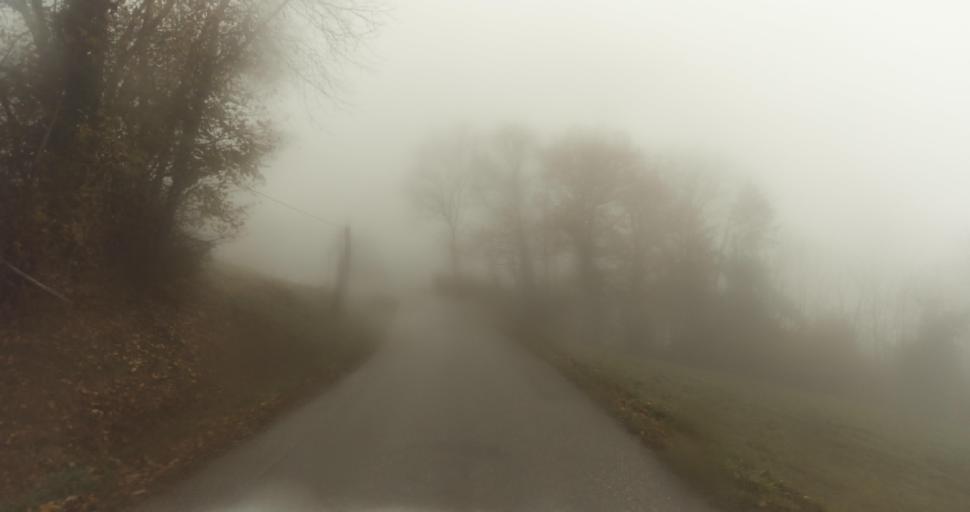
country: FR
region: Rhone-Alpes
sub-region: Departement de la Haute-Savoie
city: Villaz
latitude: 45.9740
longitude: 6.2108
